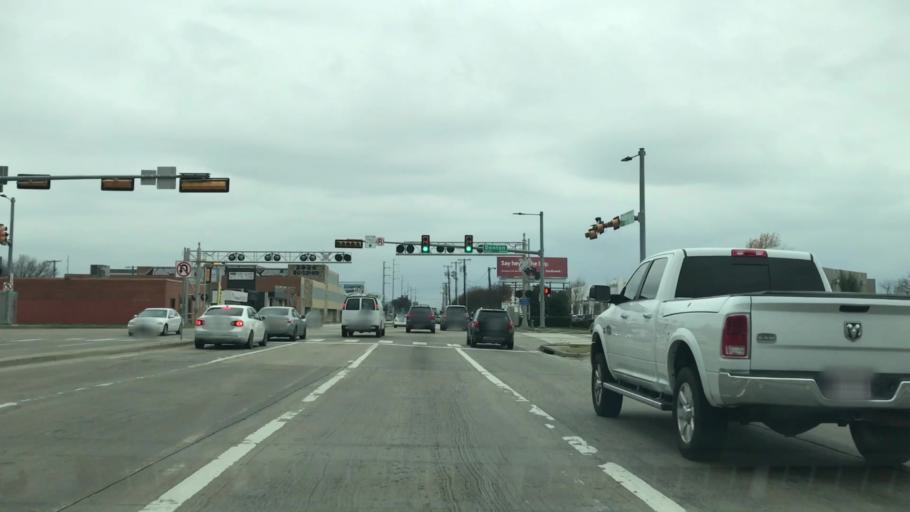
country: US
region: Texas
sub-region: Dallas County
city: University Park
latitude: 32.8306
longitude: -96.8413
